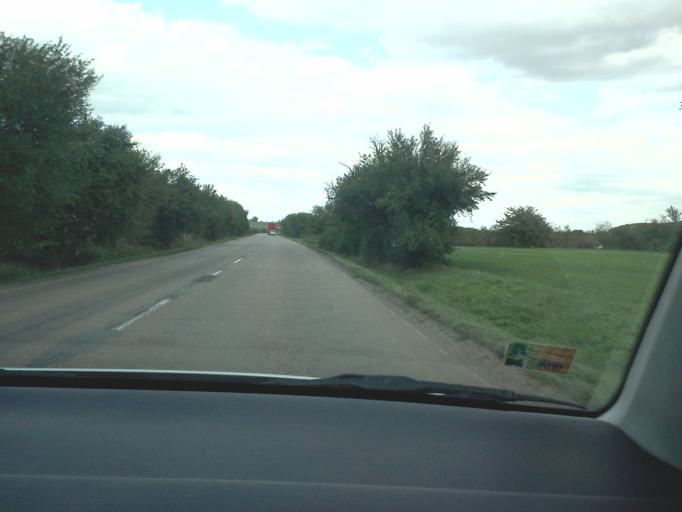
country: CZ
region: Central Bohemia
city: Prerov nad Labem
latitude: 50.1529
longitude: 14.8484
